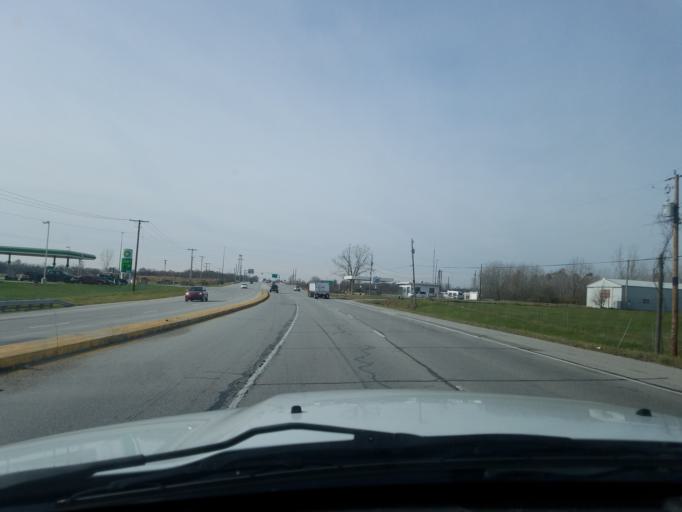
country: US
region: Indiana
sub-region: Delaware County
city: Yorktown
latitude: 40.2188
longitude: -85.5552
